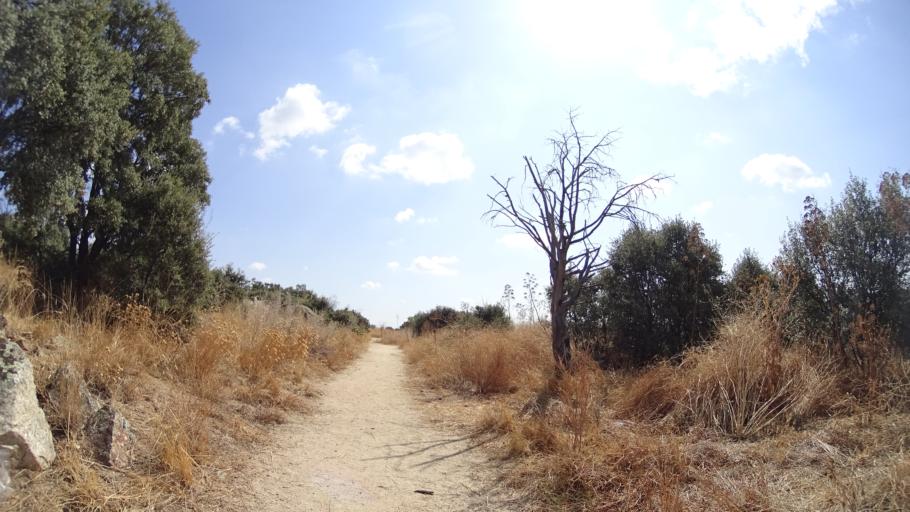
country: ES
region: Madrid
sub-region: Provincia de Madrid
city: Galapagar
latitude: 40.5823
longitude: -3.9887
